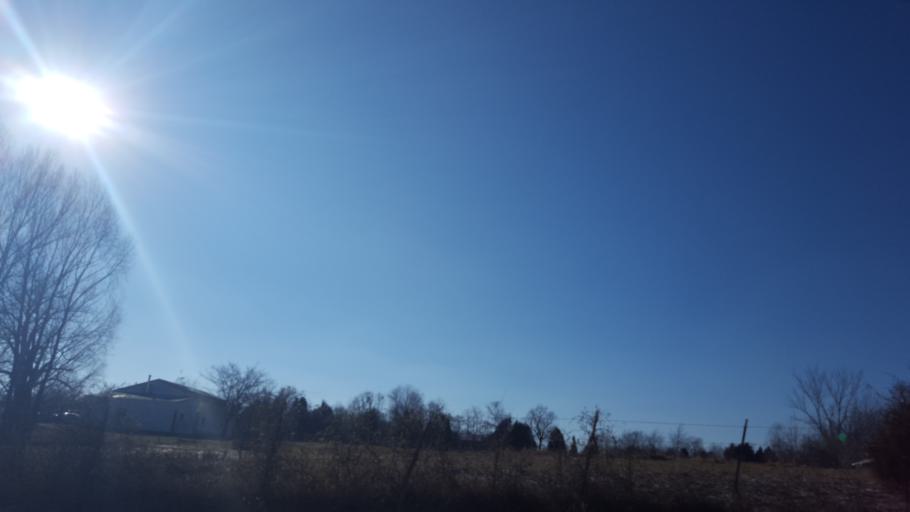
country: US
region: Kentucky
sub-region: Crittenden County
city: Marion
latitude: 37.4294
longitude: -88.0458
